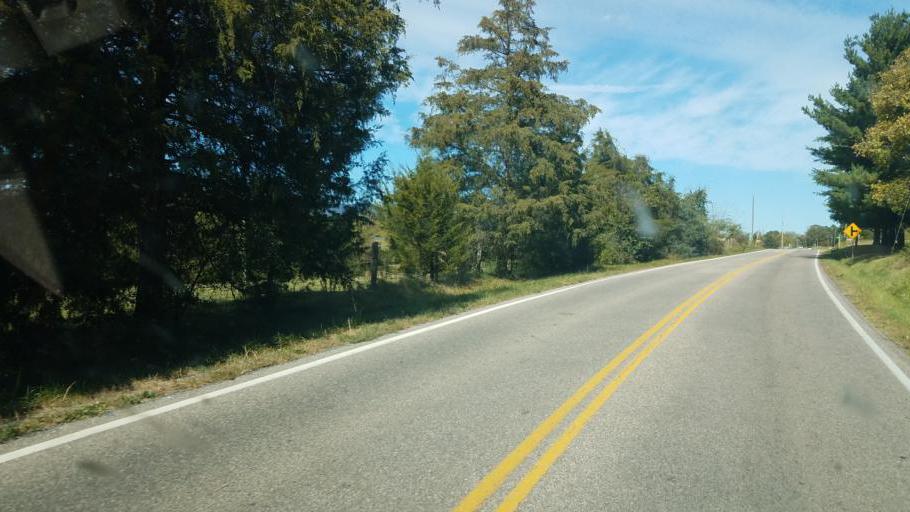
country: US
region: Virginia
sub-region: Page County
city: Shenandoah
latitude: 38.5213
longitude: -78.6164
